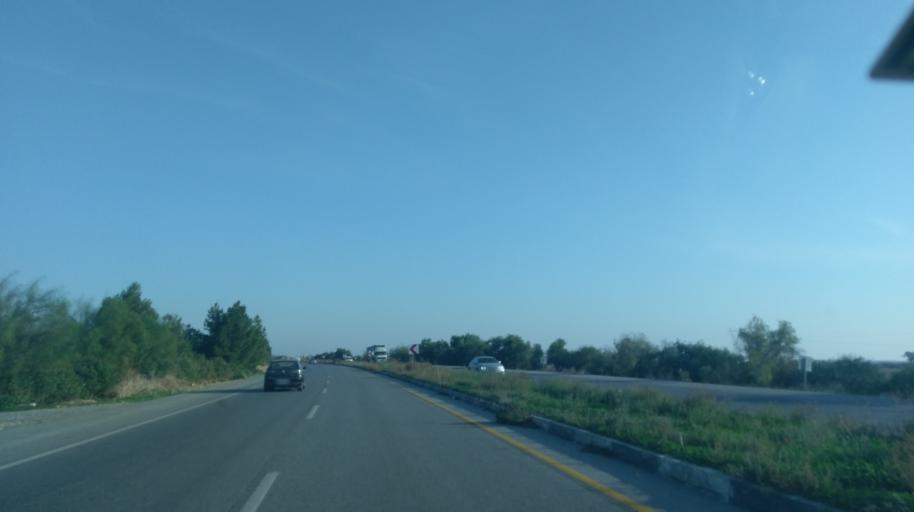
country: CY
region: Ammochostos
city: Acheritou
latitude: 35.1414
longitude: 33.8627
